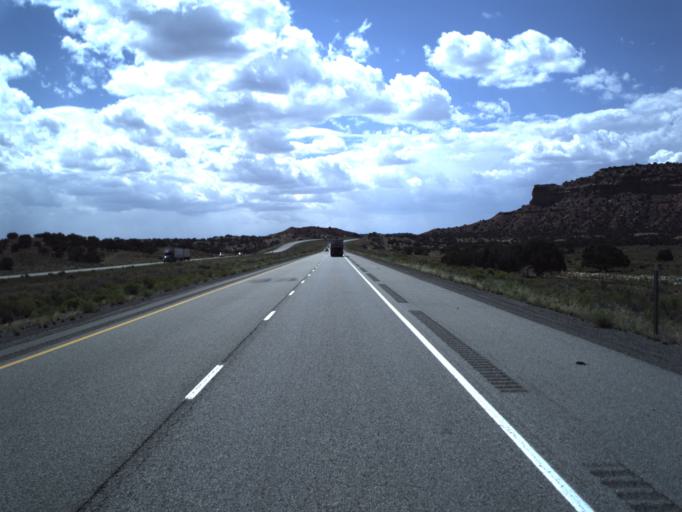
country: US
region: Utah
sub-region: Emery County
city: Castle Dale
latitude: 38.8704
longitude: -110.6938
